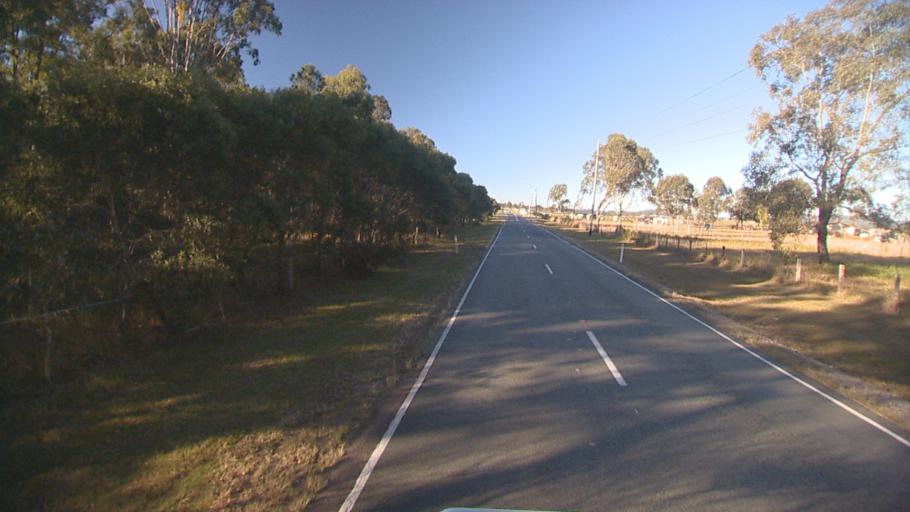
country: AU
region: Queensland
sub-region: Logan
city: Chambers Flat
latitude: -27.7542
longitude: 153.0895
